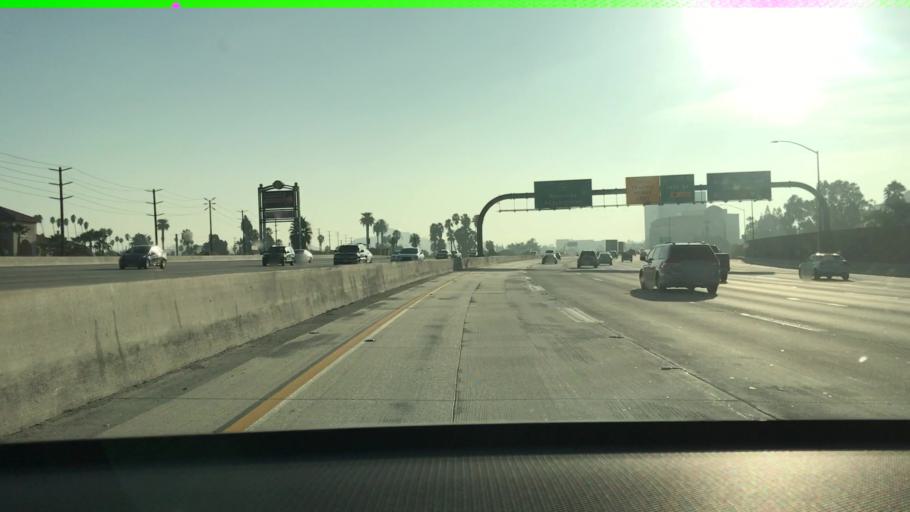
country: US
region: California
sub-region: Riverside County
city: Rubidoux
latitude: 33.9835
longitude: -117.3664
